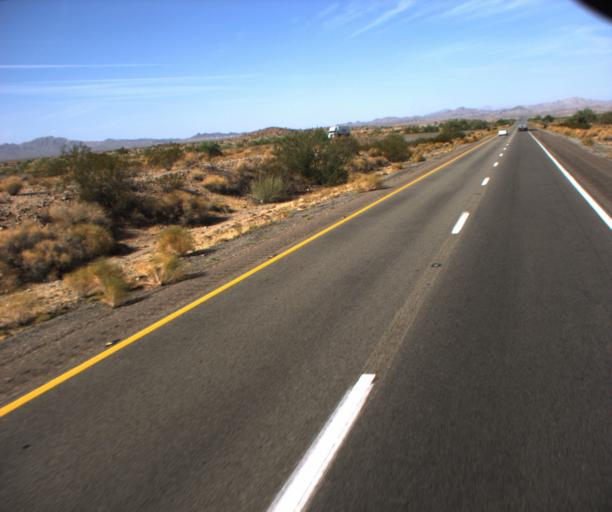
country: US
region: Arizona
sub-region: Mohave County
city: Desert Hills
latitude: 34.7499
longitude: -114.2258
